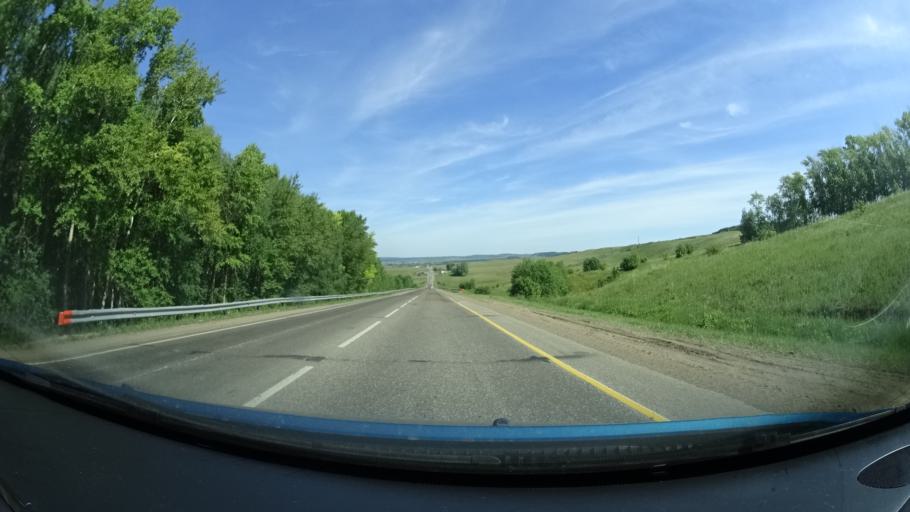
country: RU
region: Bashkortostan
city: Blagoveshchensk
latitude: 55.1609
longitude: 55.8532
